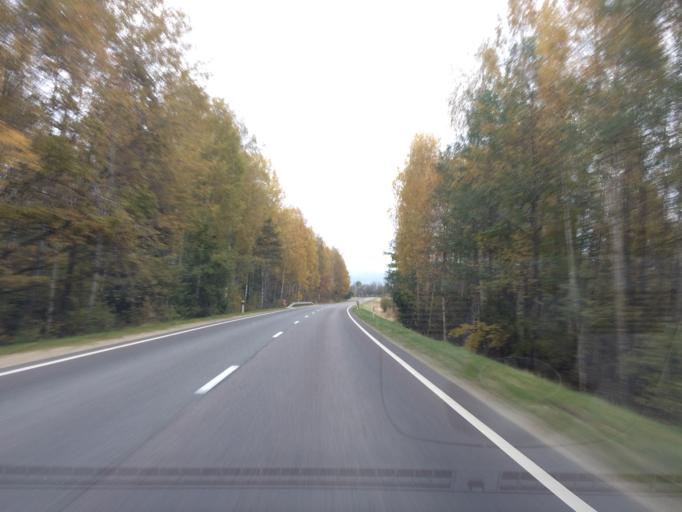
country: LV
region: Livani
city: Livani
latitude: 56.5285
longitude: 26.2047
